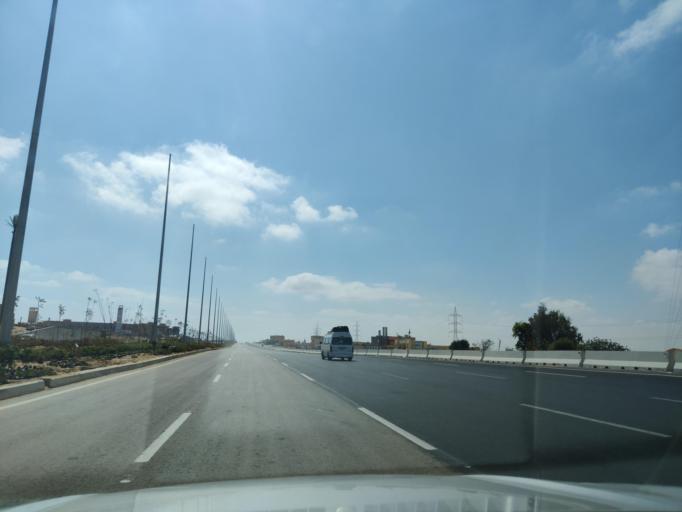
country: EG
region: Muhafazat Matruh
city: Al `Alamayn
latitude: 30.9940
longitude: 28.6630
